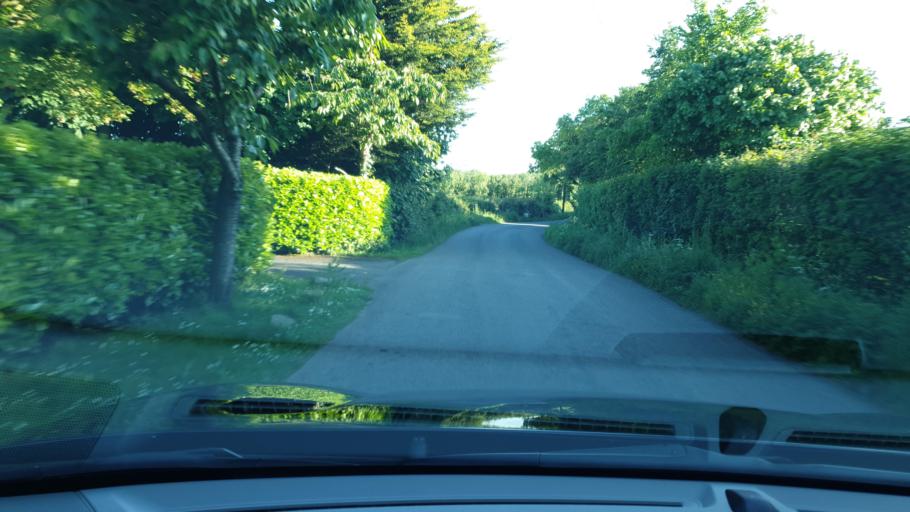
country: IE
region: Leinster
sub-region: Fingal County
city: Swords
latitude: 53.4995
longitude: -6.2293
